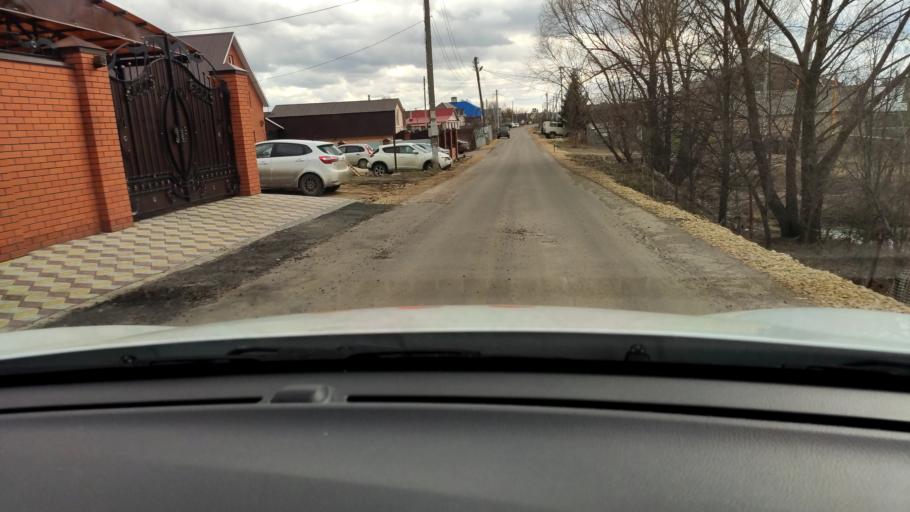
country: RU
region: Tatarstan
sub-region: Gorod Kazan'
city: Kazan
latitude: 55.8998
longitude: 49.1380
